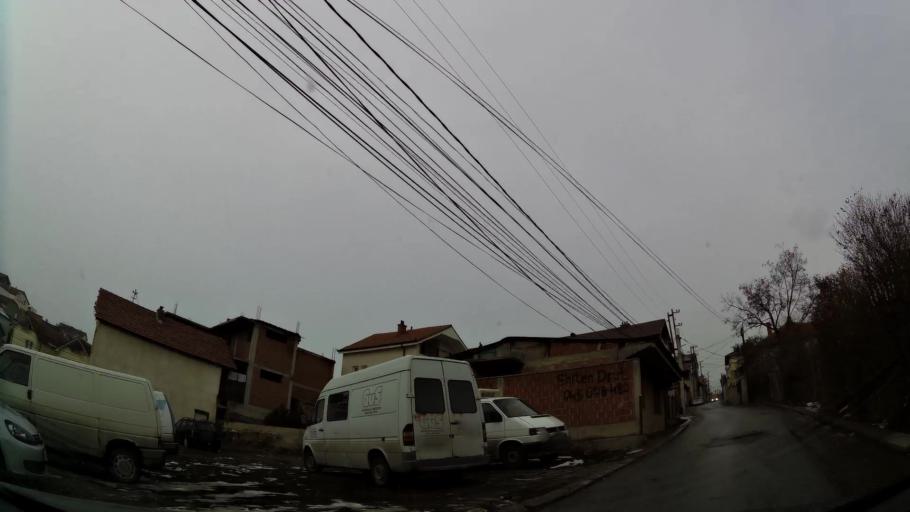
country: XK
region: Pristina
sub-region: Komuna e Prishtines
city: Pristina
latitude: 42.6798
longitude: 21.1664
